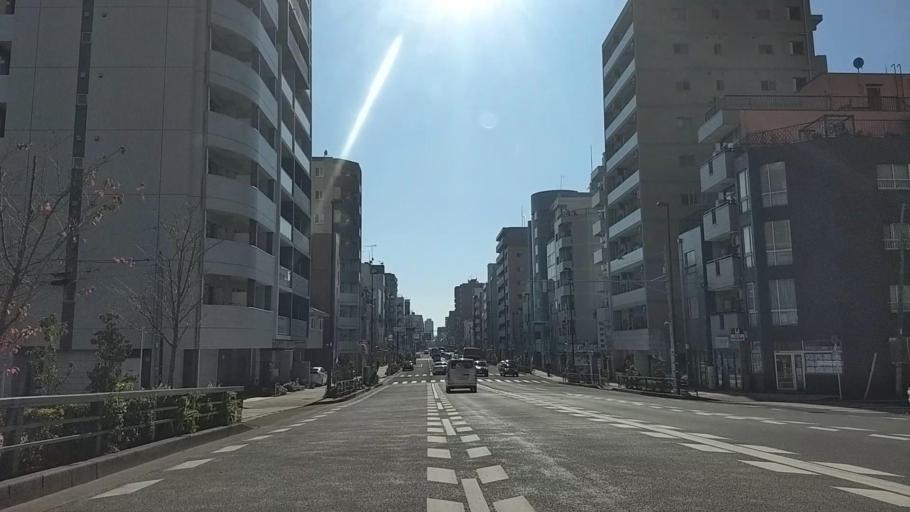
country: JP
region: Tokyo
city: Urayasu
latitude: 35.6919
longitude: 139.7979
